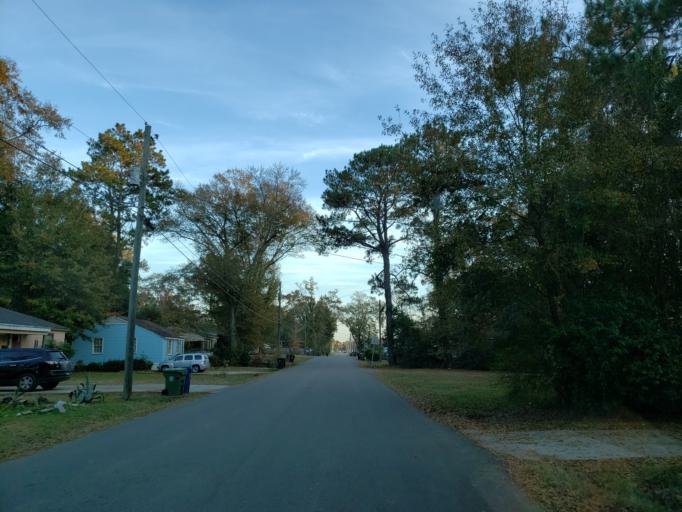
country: US
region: Mississippi
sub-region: Forrest County
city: Hattiesburg
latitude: 31.3167
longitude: -89.3125
